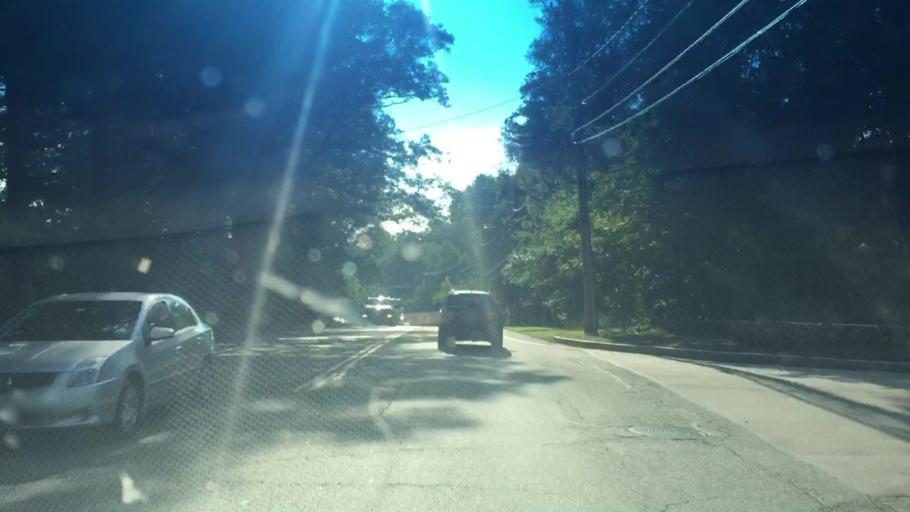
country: US
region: Massachusetts
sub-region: Norfolk County
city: Medfield
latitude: 42.1964
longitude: -71.2850
